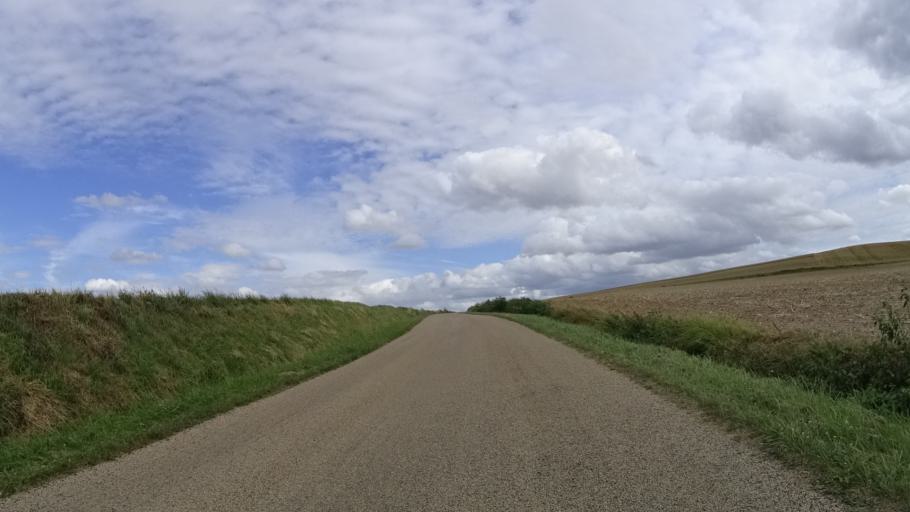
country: FR
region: Bourgogne
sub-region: Departement de l'Yonne
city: Cezy
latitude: 47.9827
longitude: 3.2939
